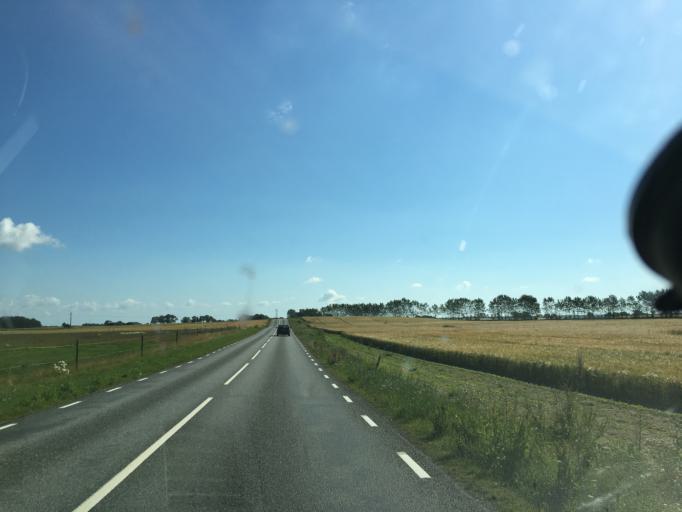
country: SE
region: Skane
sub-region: Kristianstads Kommun
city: Norra Asum
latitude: 55.9525
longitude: 14.1646
